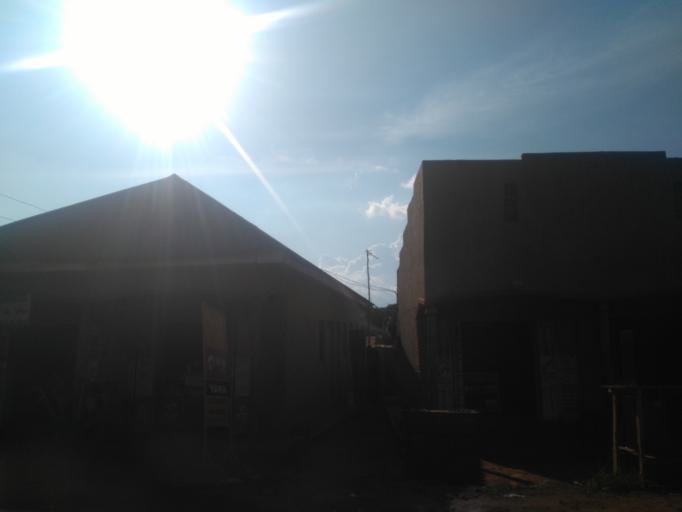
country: UG
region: Central Region
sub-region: Wakiso District
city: Kajansi
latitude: 0.2674
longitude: 32.4719
